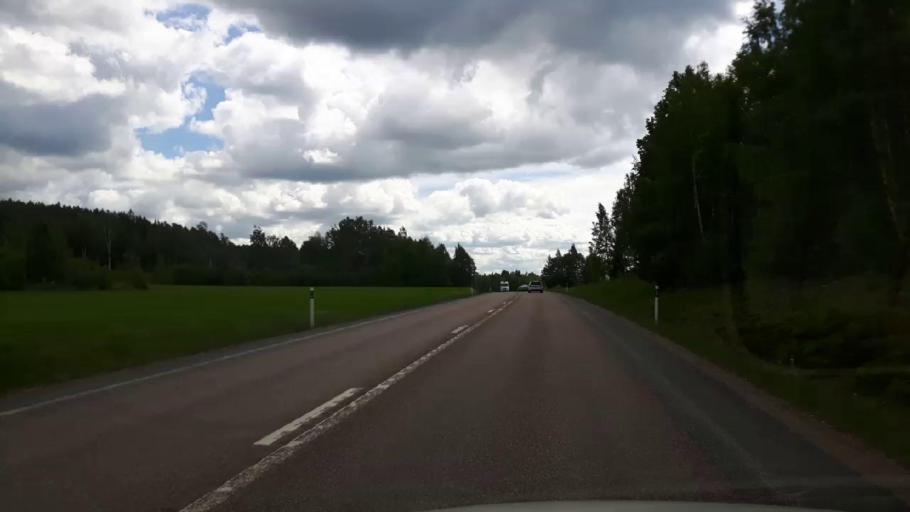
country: SE
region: Dalarna
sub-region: Saters Kommun
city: Saeter
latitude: 60.4847
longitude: 15.7702
